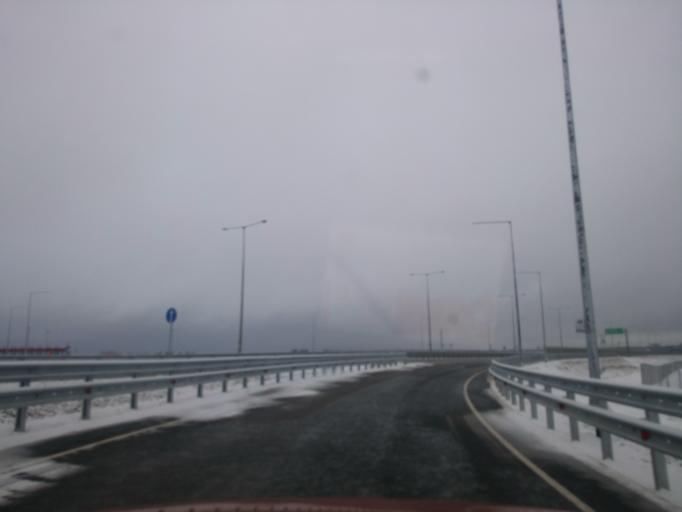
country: RU
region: Tverskaya
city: Likhoslavl'
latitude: 56.9810
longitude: 35.4234
